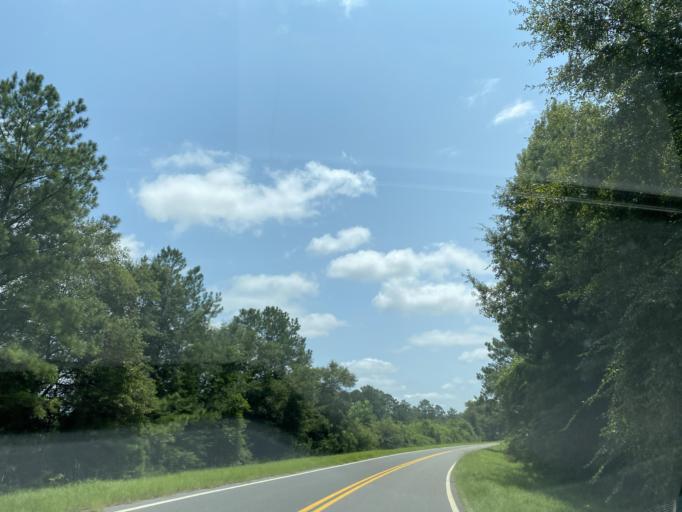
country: US
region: Georgia
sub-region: Telfair County
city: Lumber City
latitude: 31.9629
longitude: -82.7010
